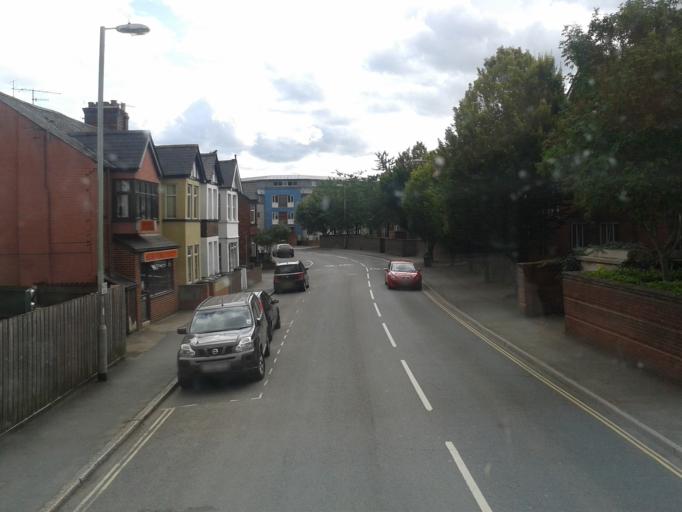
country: GB
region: England
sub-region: Devon
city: Exeter
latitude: 50.7285
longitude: -3.5424
